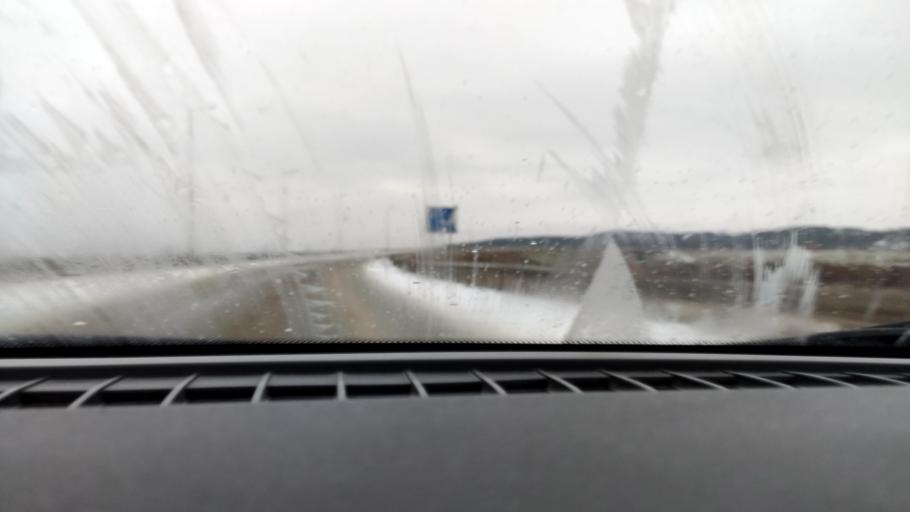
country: RU
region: Perm
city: Kondratovo
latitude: 57.9259
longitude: 56.1738
